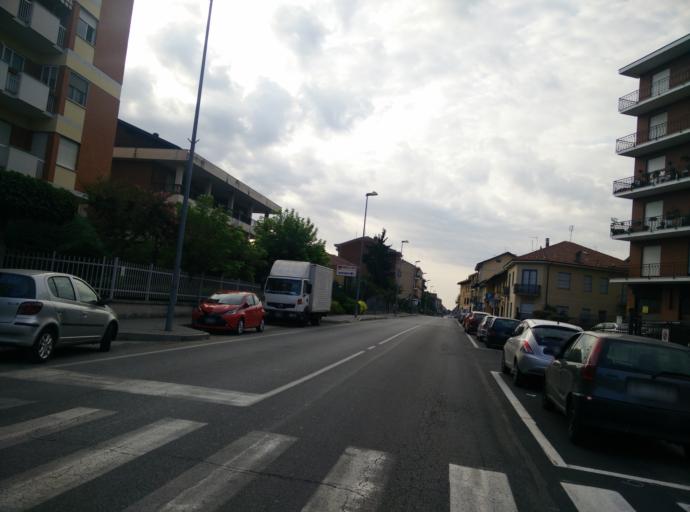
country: IT
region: Piedmont
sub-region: Provincia di Torino
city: Moncalieri
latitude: 44.9976
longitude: 7.7030
